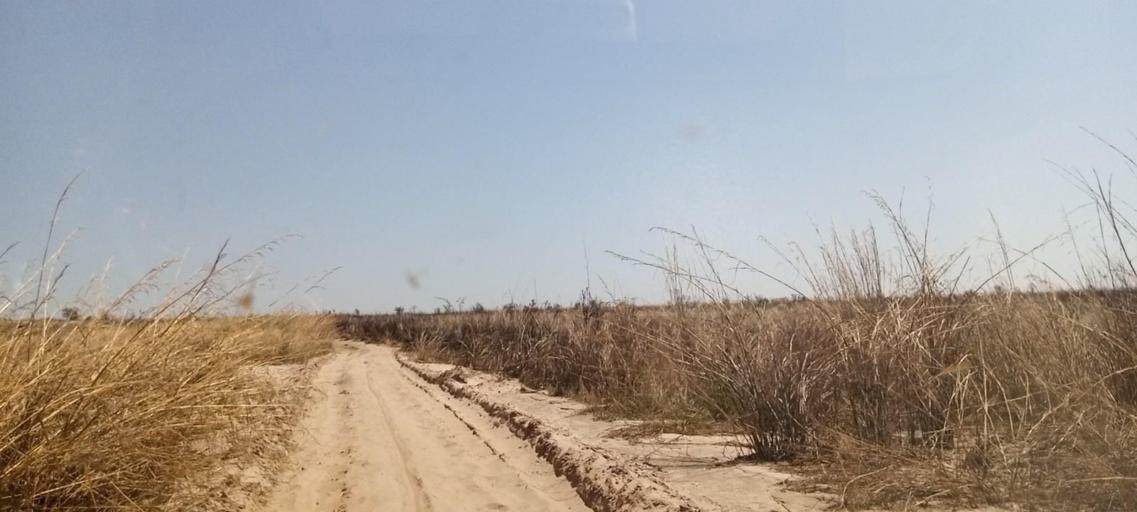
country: CD
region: Kasai-Oriental
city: Kabinda
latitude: -5.9398
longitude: 24.8111
